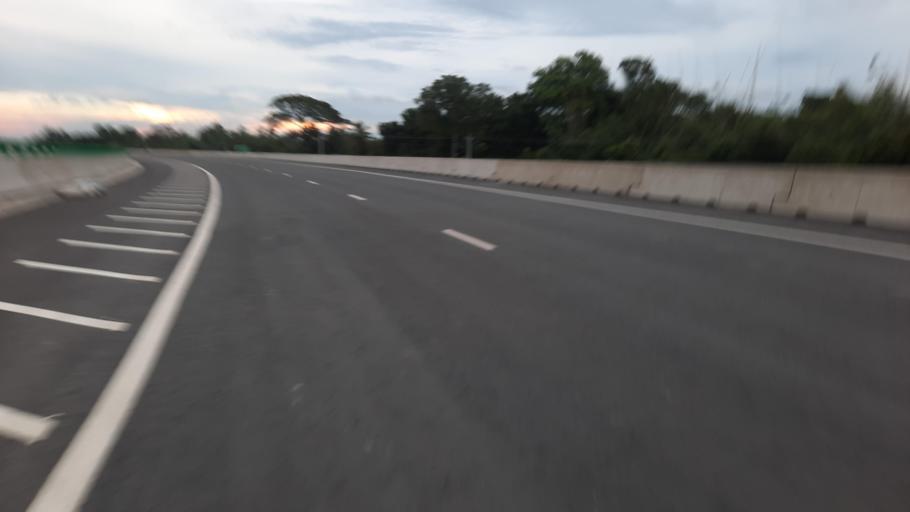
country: BD
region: Khulna
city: Kalia
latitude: 23.1892
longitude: 89.7013
